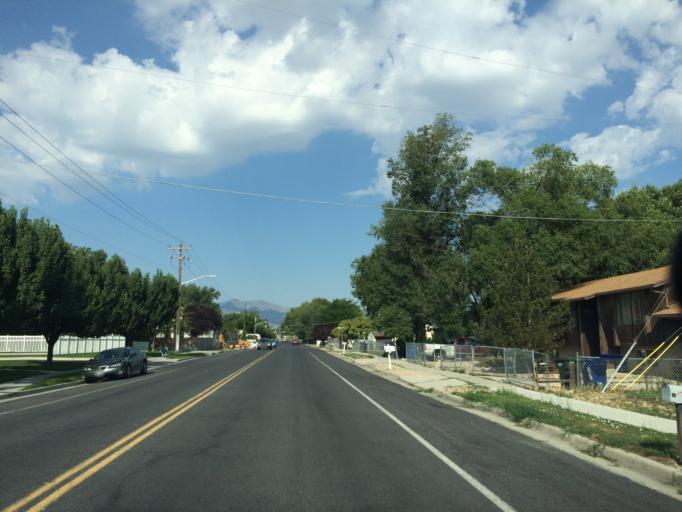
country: US
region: Utah
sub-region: Salt Lake County
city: West Valley City
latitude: 40.6929
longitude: -111.9713
